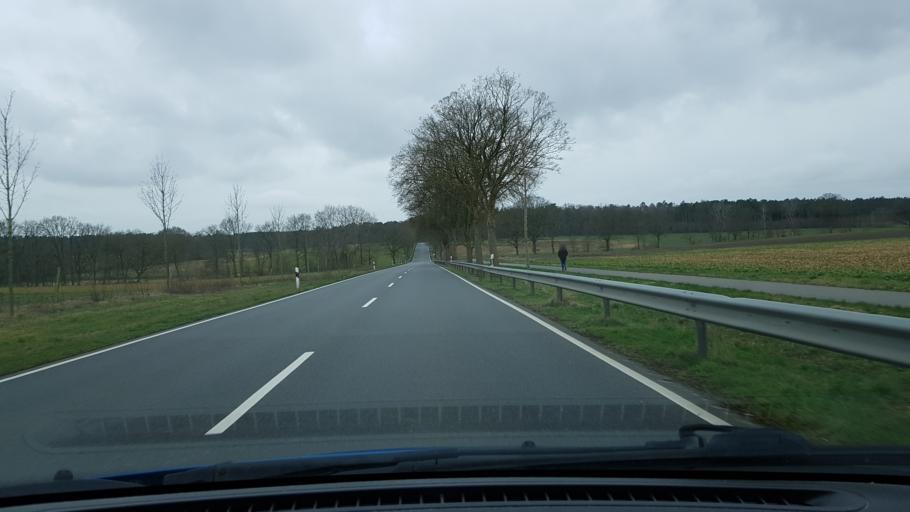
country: DE
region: Lower Saxony
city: Stoetze
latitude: 53.0493
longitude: 10.8085
